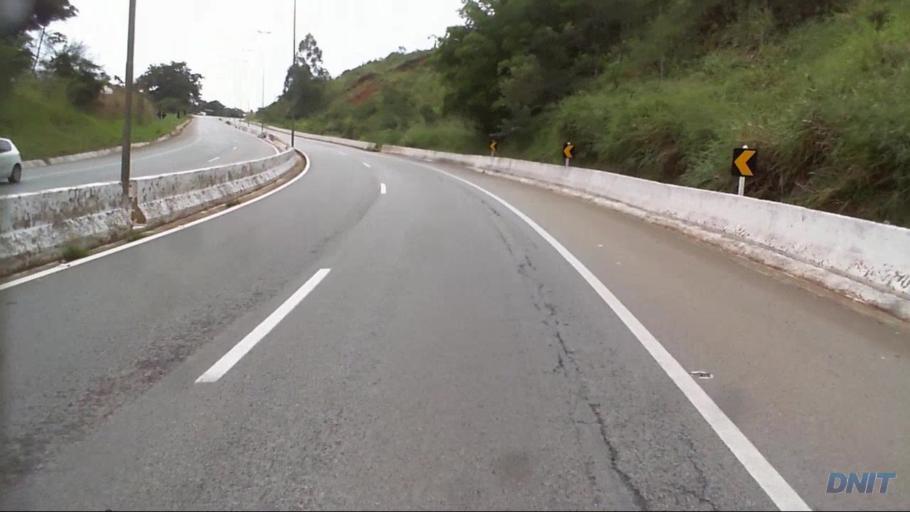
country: BR
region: Minas Gerais
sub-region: Nova Era
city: Nova Era
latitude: -19.7599
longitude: -43.0350
